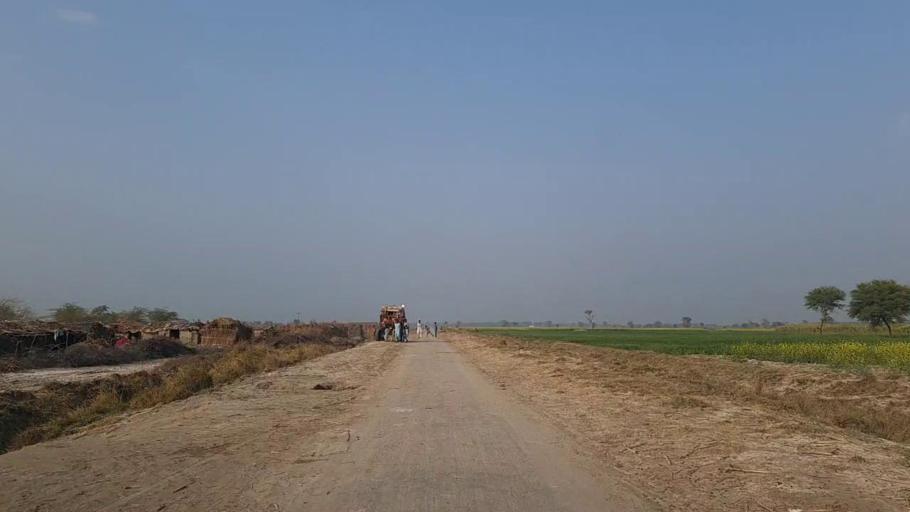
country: PK
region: Sindh
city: Jam Sahib
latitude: 26.3331
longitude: 68.5147
